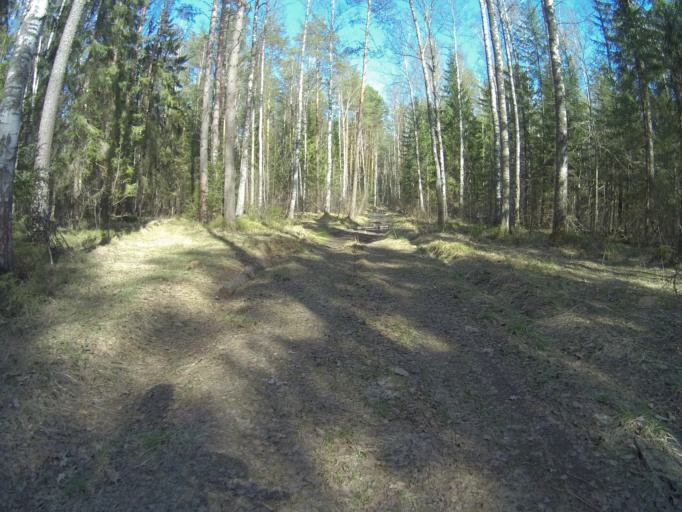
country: RU
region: Vladimir
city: Orgtrud
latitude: 56.1257
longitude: 40.5733
